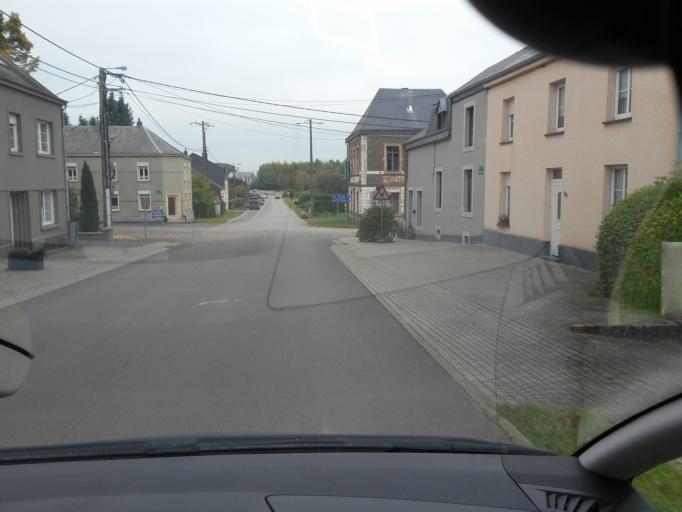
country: BE
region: Wallonia
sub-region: Province du Luxembourg
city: Attert
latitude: 49.7210
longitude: 5.7966
